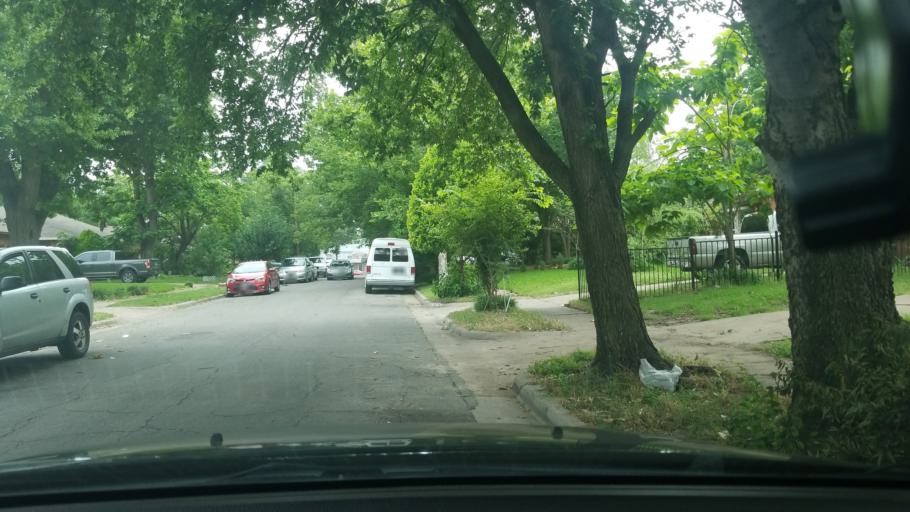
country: US
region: Texas
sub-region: Dallas County
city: Balch Springs
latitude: 32.7536
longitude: -96.6926
